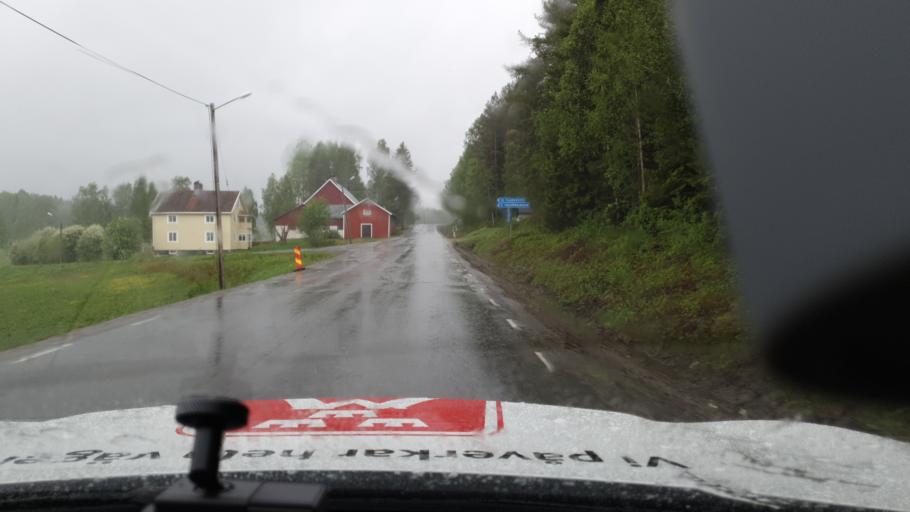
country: SE
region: Vaesterbotten
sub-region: Umea Kommun
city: Roback
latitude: 64.0268
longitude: 20.0872
